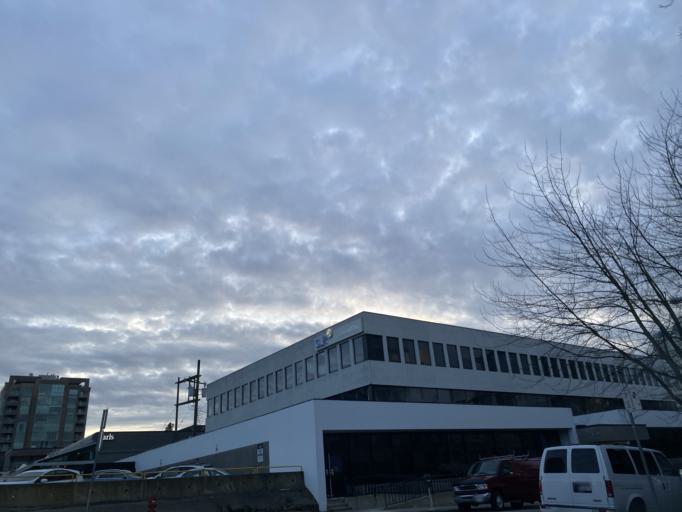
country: CA
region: British Columbia
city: West End
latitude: 49.2647
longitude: -123.1411
